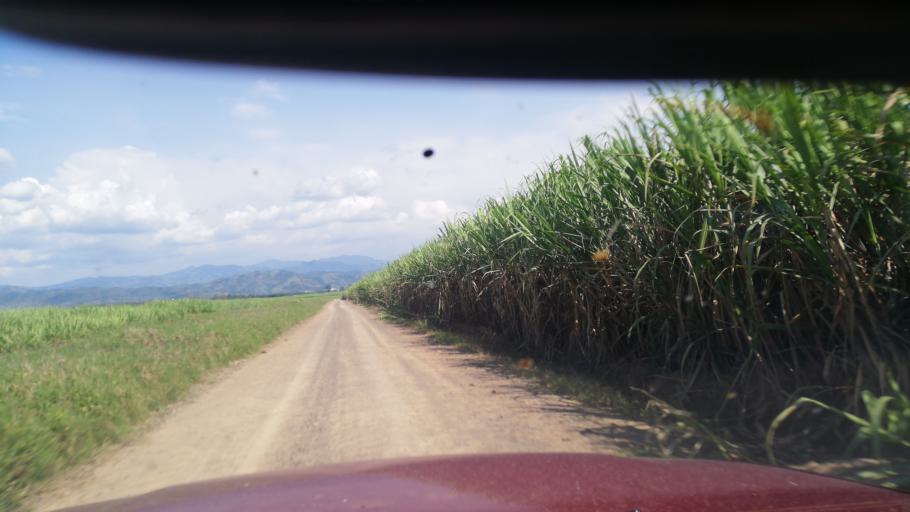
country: CO
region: Risaralda
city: La Virginia
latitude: 4.8924
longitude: -75.9253
